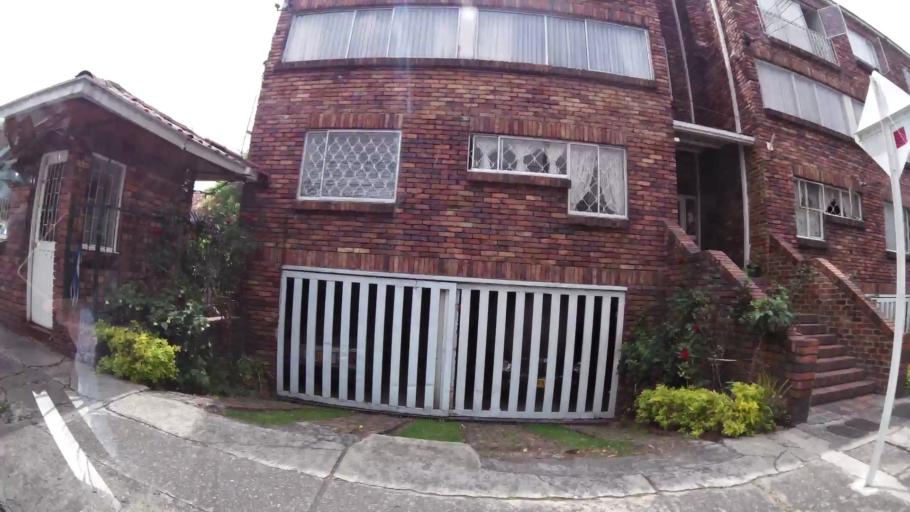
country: CO
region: Bogota D.C.
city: Barrio San Luis
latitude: 4.6835
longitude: -74.0698
